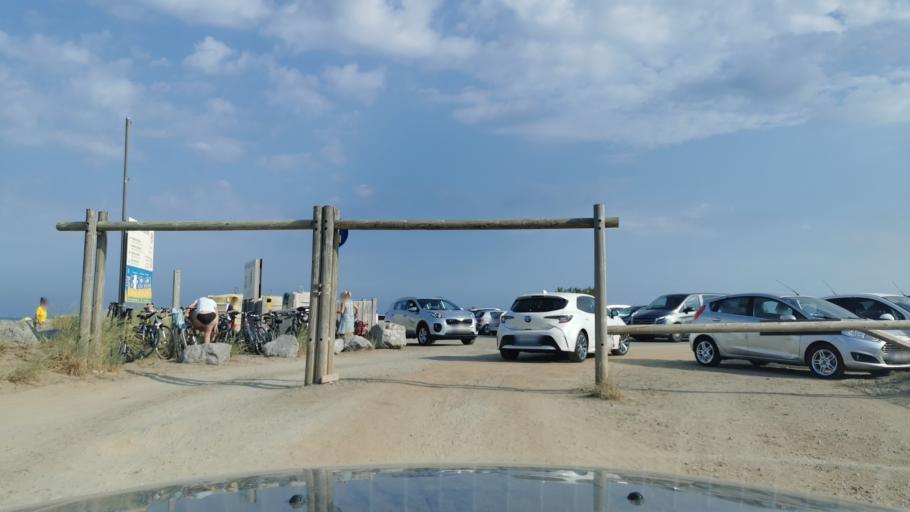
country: FR
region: Languedoc-Roussillon
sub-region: Departement de l'Aude
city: Gruissan
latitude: 43.1155
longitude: 3.1276
